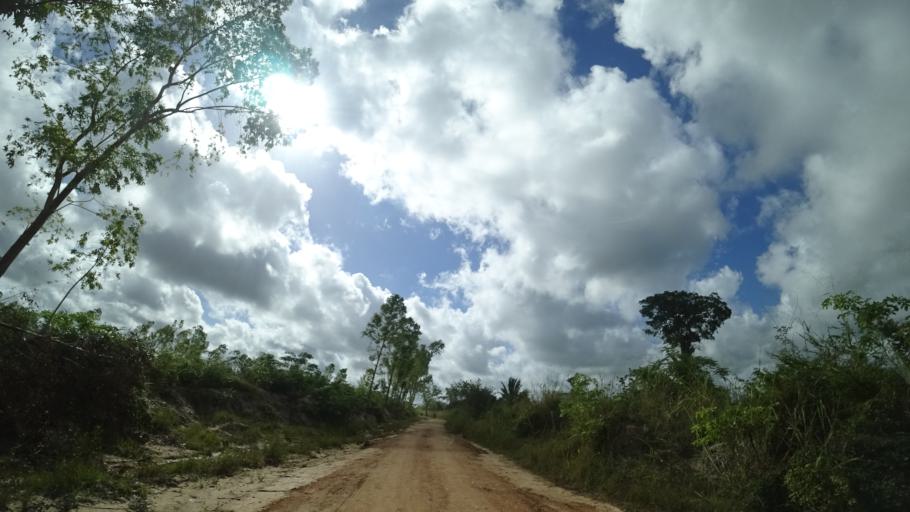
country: MZ
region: Sofala
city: Dondo
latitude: -19.4239
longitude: 34.7099
